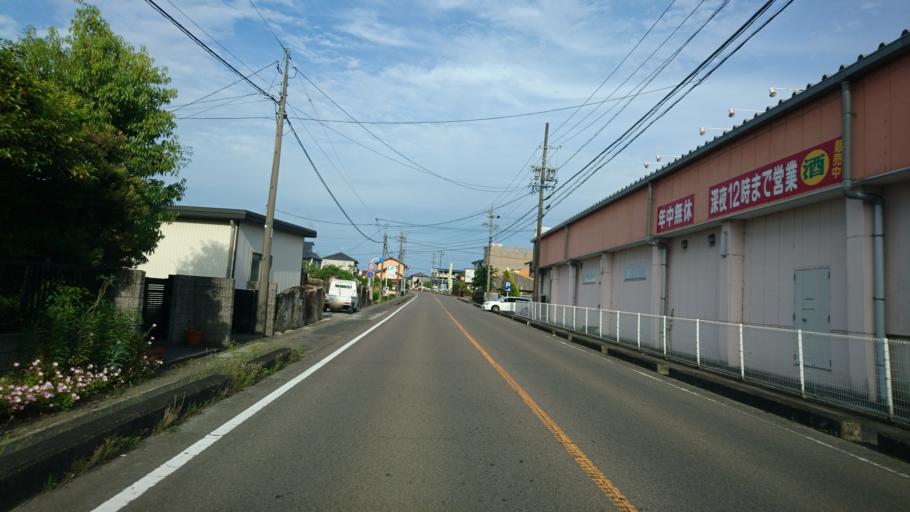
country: JP
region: Gifu
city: Minokamo
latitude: 35.4362
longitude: 137.0468
